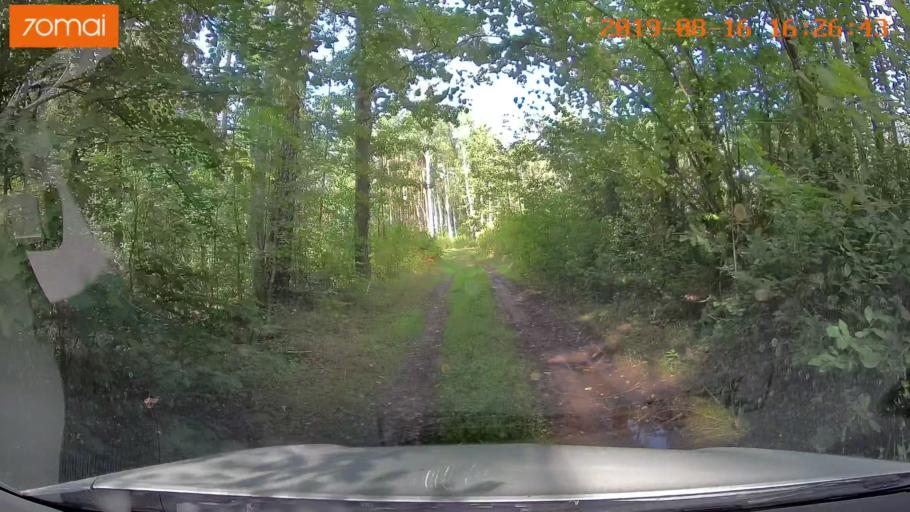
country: BY
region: Mogilev
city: Asipovichy
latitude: 53.2233
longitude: 28.7683
